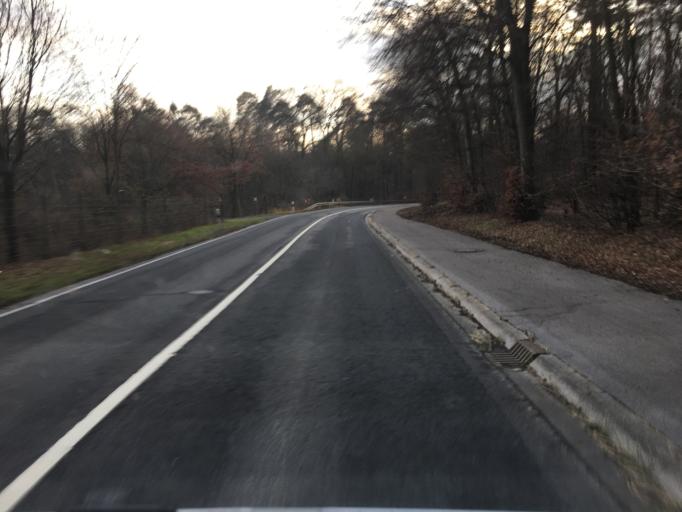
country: DE
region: North Rhine-Westphalia
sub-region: Regierungsbezirk Koln
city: Rosrath
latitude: 50.9144
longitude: 7.1518
